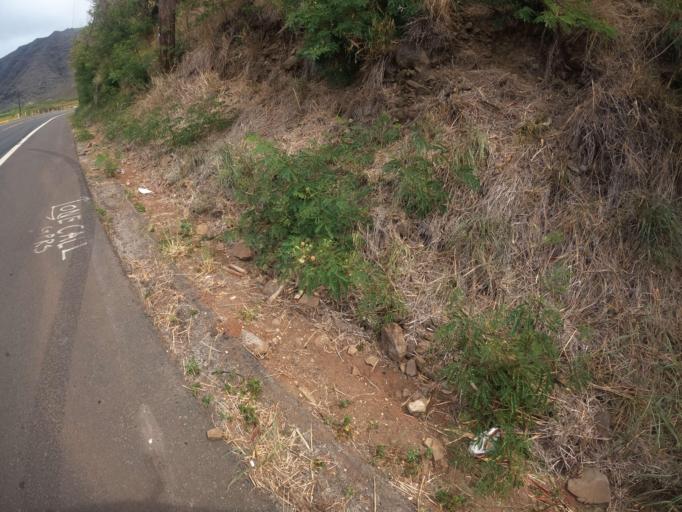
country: US
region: Hawaii
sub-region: Honolulu County
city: Makaha Valley
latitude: 21.5199
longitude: -158.2278
